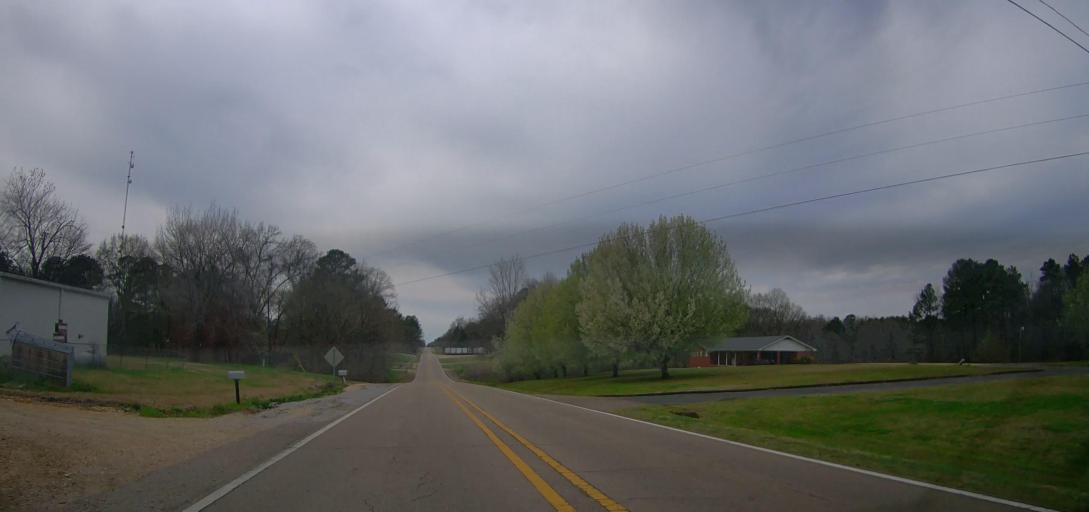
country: US
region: Mississippi
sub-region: Itawamba County
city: Mantachie
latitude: 34.2589
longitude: -88.5118
